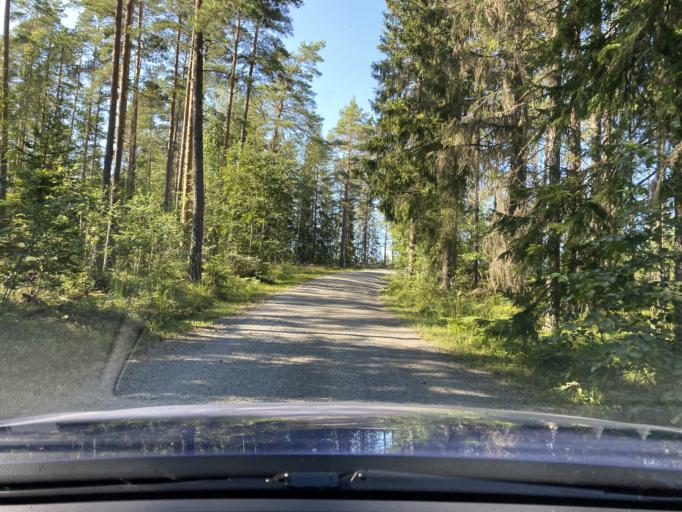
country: FI
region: Satakunta
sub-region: Rauma
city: Kiukainen
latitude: 61.1434
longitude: 22.0233
